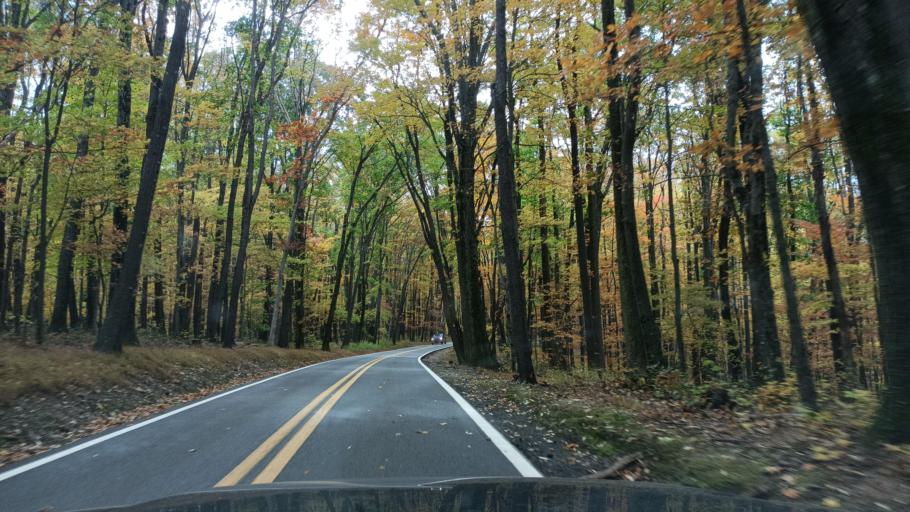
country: US
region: West Virginia
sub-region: Monongalia County
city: Cheat Lake
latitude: 39.6509
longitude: -79.7846
